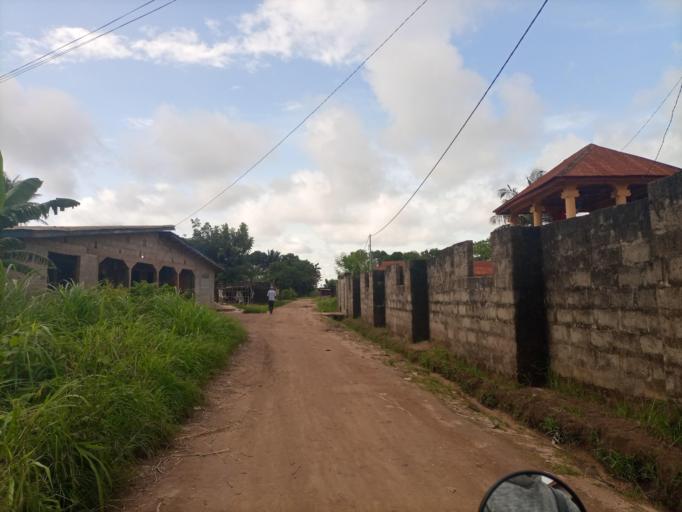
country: SL
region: Northern Province
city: Masoyila
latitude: 8.6086
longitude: -13.1831
